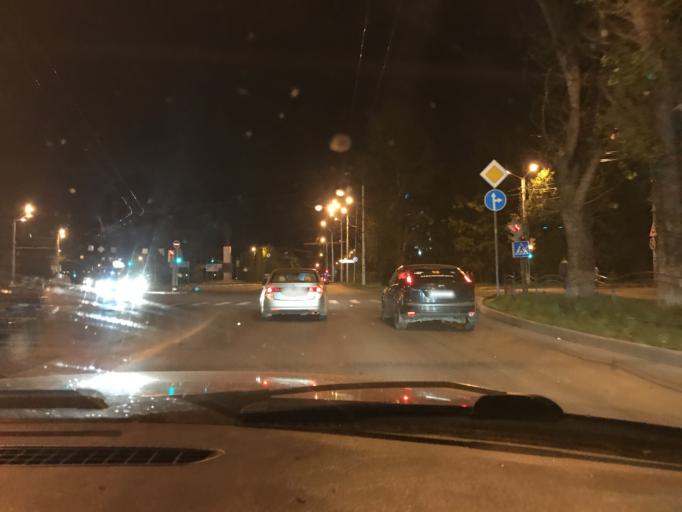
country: RU
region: Kaluga
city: Kaluga
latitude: 54.5298
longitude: 36.2697
